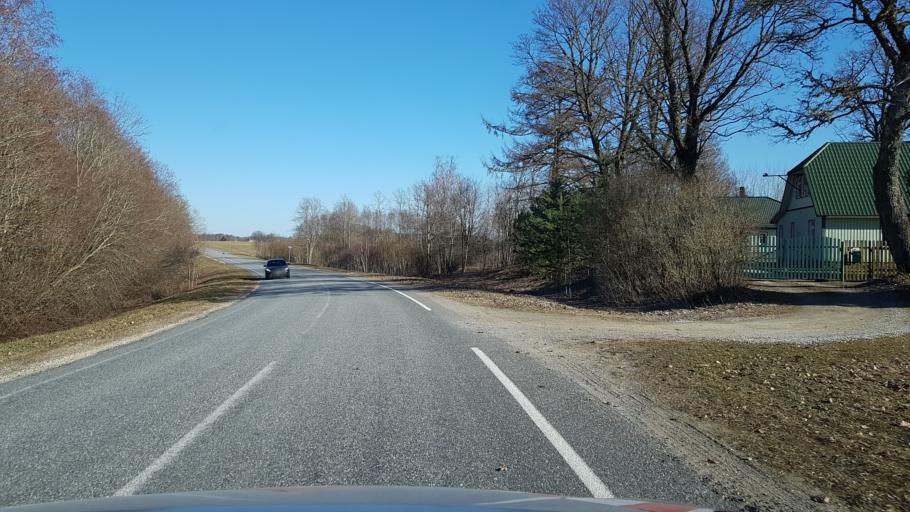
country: EE
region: Laeaene-Virumaa
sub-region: Haljala vald
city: Haljala
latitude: 59.4643
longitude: 26.1857
